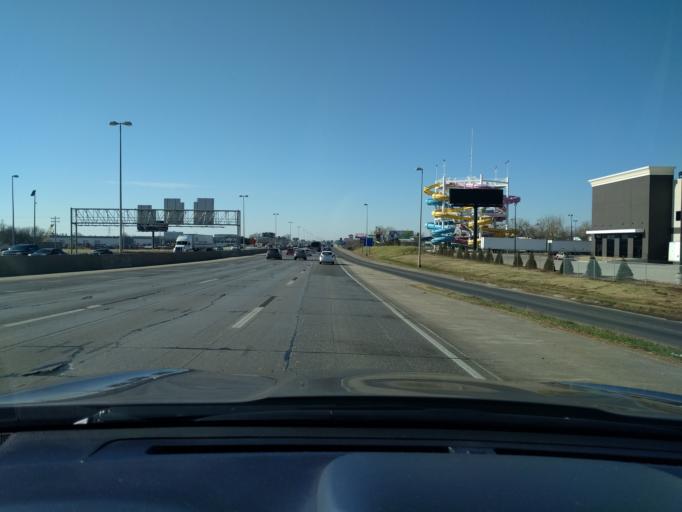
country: US
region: Oklahoma
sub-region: Oklahoma County
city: Oklahoma City
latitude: 35.4602
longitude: -97.5857
